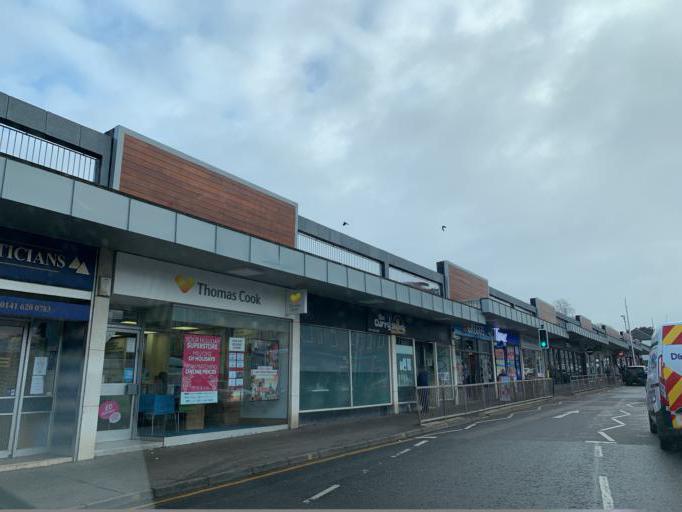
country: GB
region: Scotland
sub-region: East Renfrewshire
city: Clarkston
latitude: 55.7901
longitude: -4.2774
